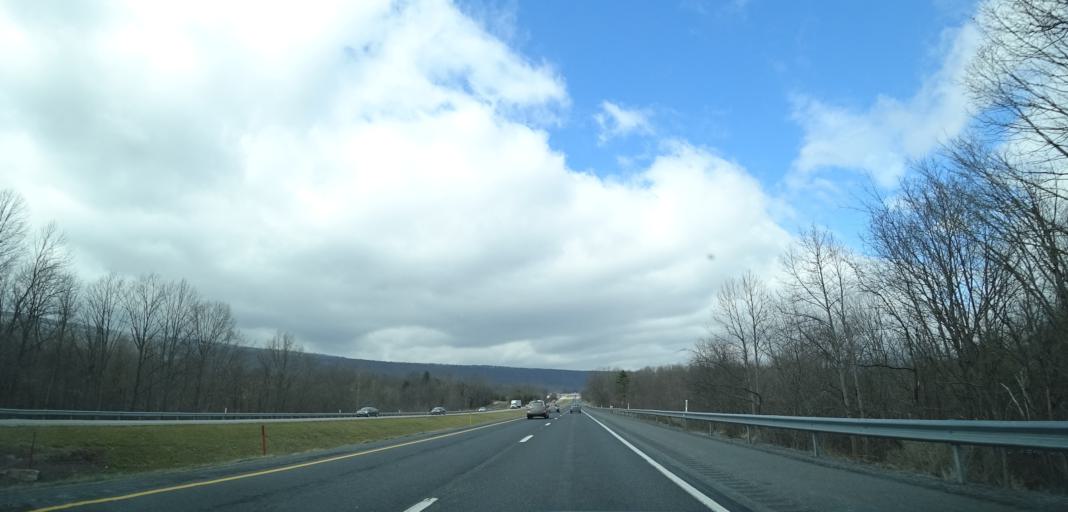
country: US
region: Maryland
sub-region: Washington County
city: Hancock
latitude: 39.8208
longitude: -78.2717
